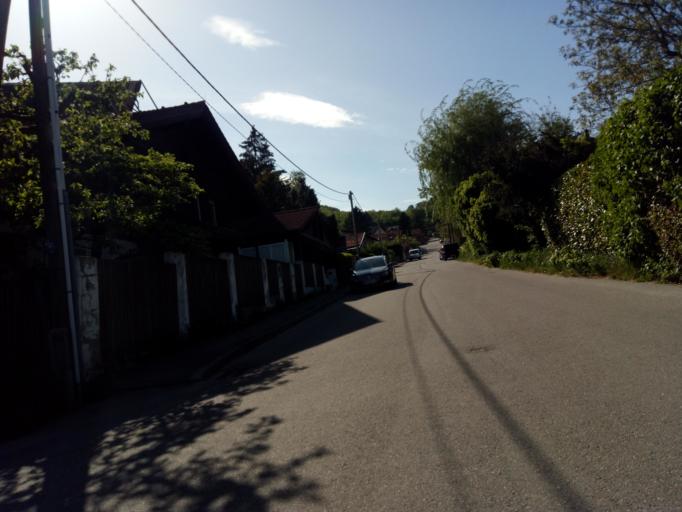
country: AT
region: Lower Austria
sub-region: Politischer Bezirk Modling
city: Laab im Walde
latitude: 48.1394
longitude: 16.1900
